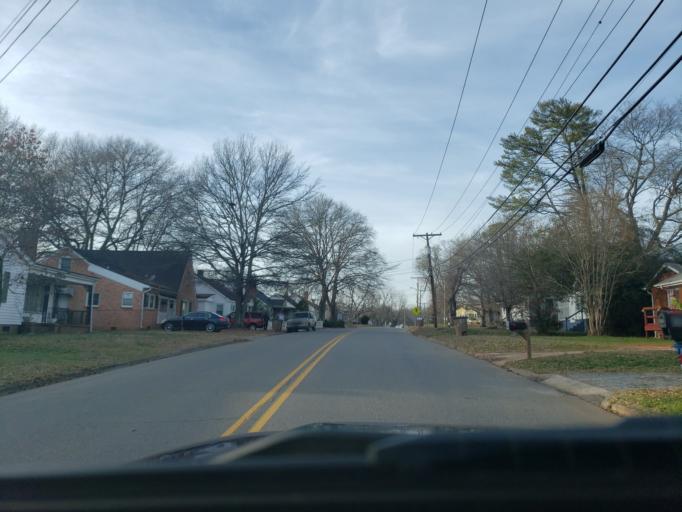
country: US
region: North Carolina
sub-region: Cleveland County
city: Shelby
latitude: 35.2845
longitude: -81.5273
